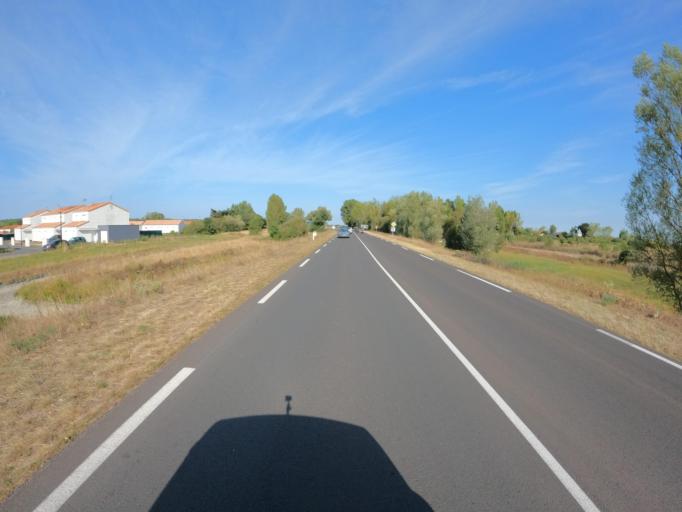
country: FR
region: Pays de la Loire
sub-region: Departement de la Vendee
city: Saint-Jean-de-Monts
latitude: 46.8008
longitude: -2.0641
